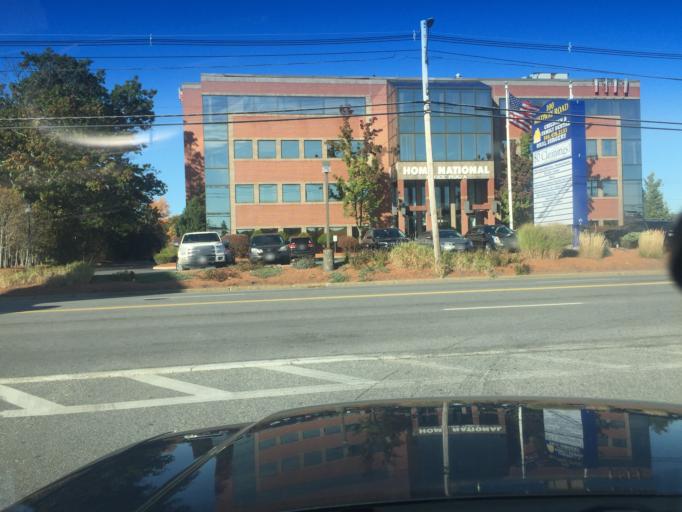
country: US
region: Massachusetts
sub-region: Worcester County
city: Milford
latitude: 42.1480
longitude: -71.4902
